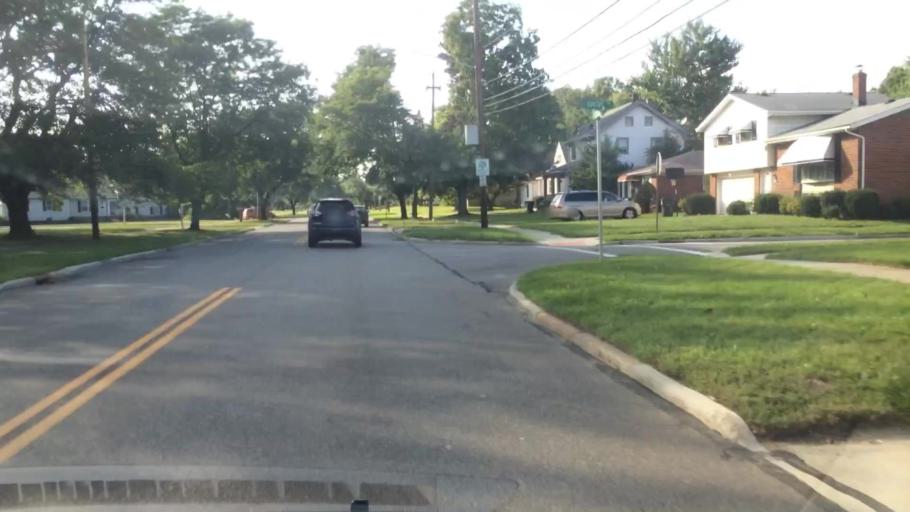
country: US
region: Ohio
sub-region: Cuyahoga County
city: Valley View
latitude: 41.3952
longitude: -81.5852
